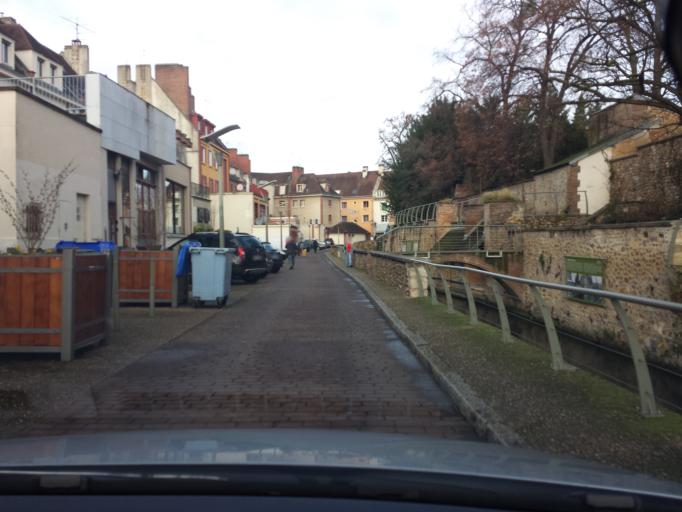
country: FR
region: Haute-Normandie
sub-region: Departement de l'Eure
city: Evreux
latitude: 49.0250
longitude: 1.1491
